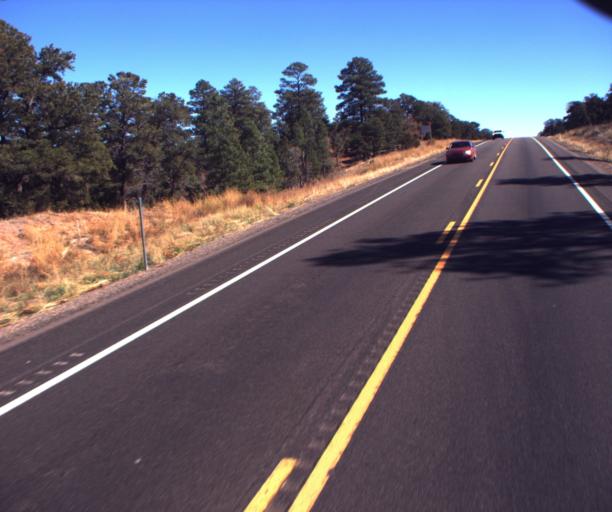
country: US
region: Arizona
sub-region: Apache County
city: Saint Michaels
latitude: 35.7066
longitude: -109.3129
